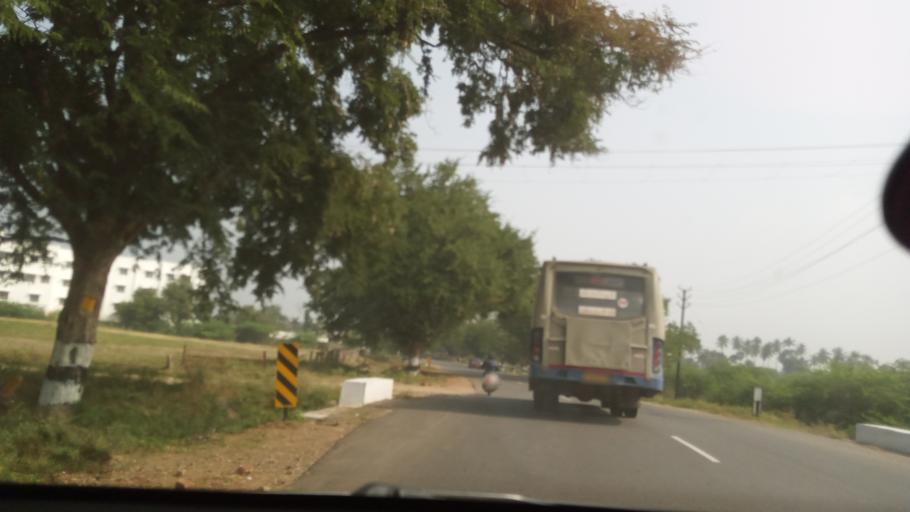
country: IN
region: Tamil Nadu
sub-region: Erode
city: Punjai Puliyampatti
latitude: 11.4231
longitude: 77.1944
